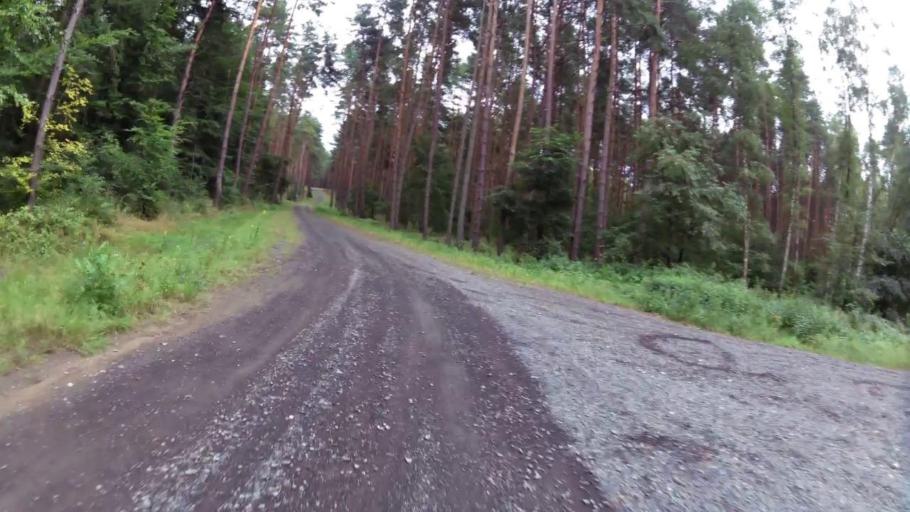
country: PL
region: West Pomeranian Voivodeship
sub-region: Powiat mysliborski
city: Debno
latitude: 52.7871
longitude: 14.7180
